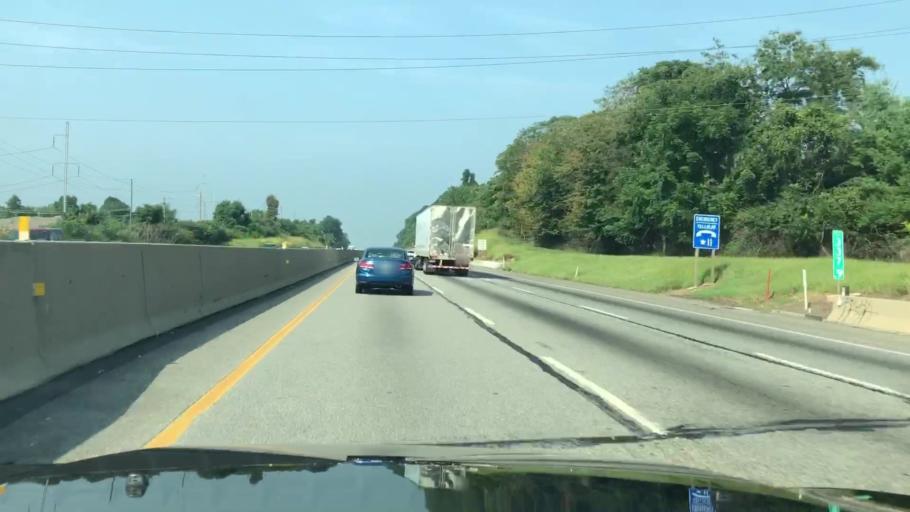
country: US
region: Pennsylvania
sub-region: Montgomery County
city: Fort Washington
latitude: 40.1297
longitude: -75.2054
